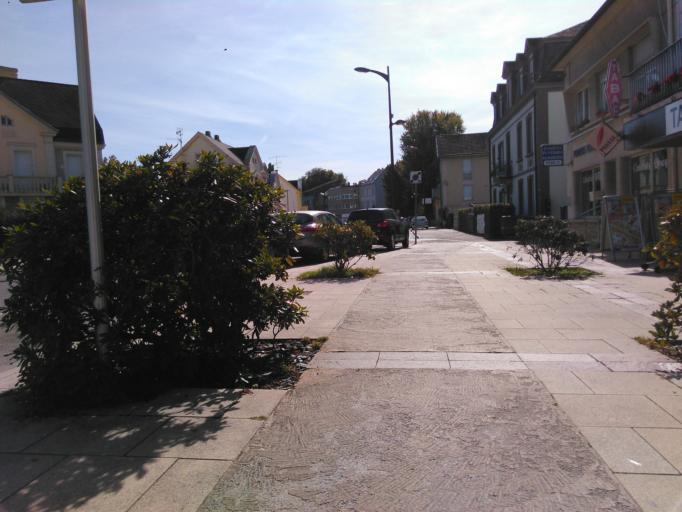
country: FR
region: Lorraine
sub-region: Departement de la Moselle
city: Thionville
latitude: 49.3666
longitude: 6.1688
